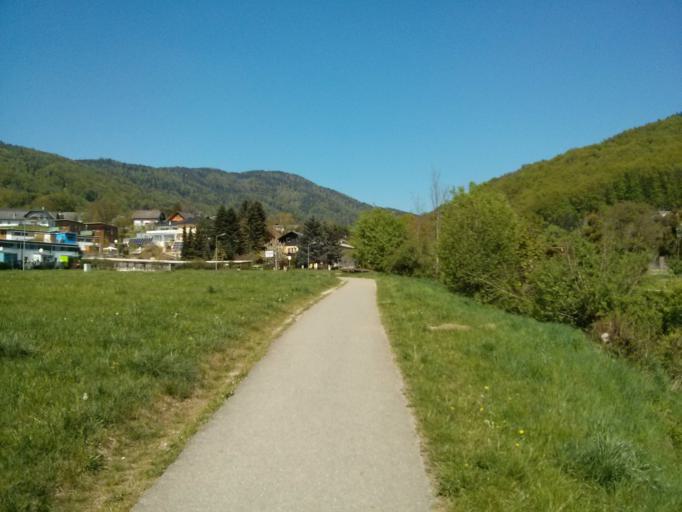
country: AT
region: Styria
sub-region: Politischer Bezirk Graz-Umgebung
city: Stattegg
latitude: 47.1404
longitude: 15.4189
